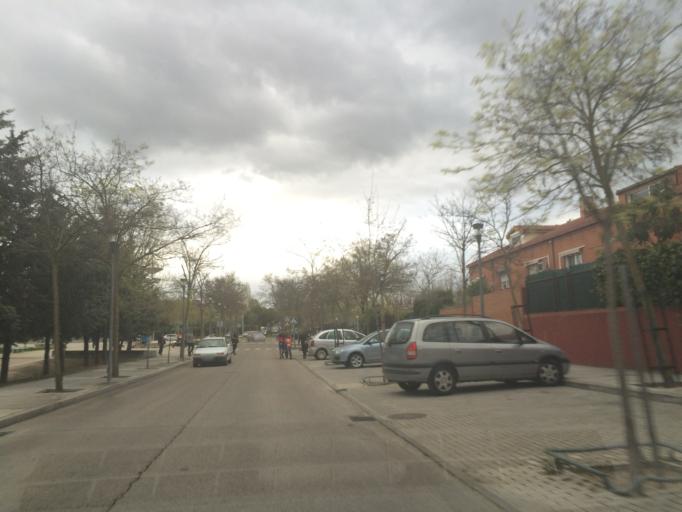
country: ES
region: Madrid
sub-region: Provincia de Madrid
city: Tres Cantos
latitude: 40.6019
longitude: -3.7054
